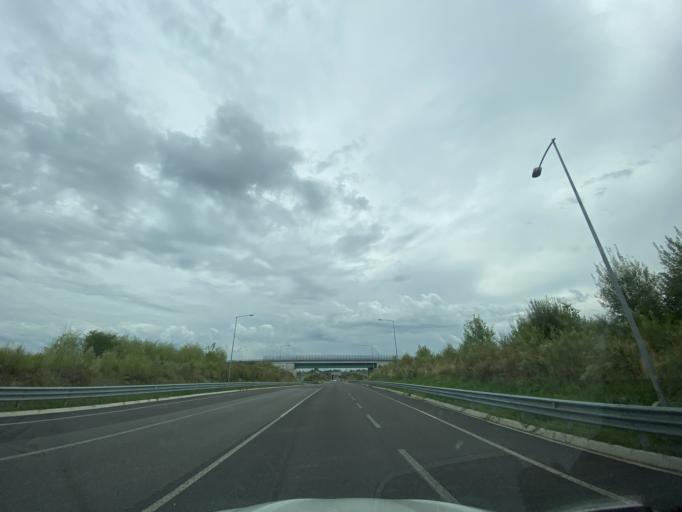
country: IT
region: Lombardy
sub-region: Provincia di Monza e Brianza
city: Caponago
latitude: 45.5601
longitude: 9.3822
